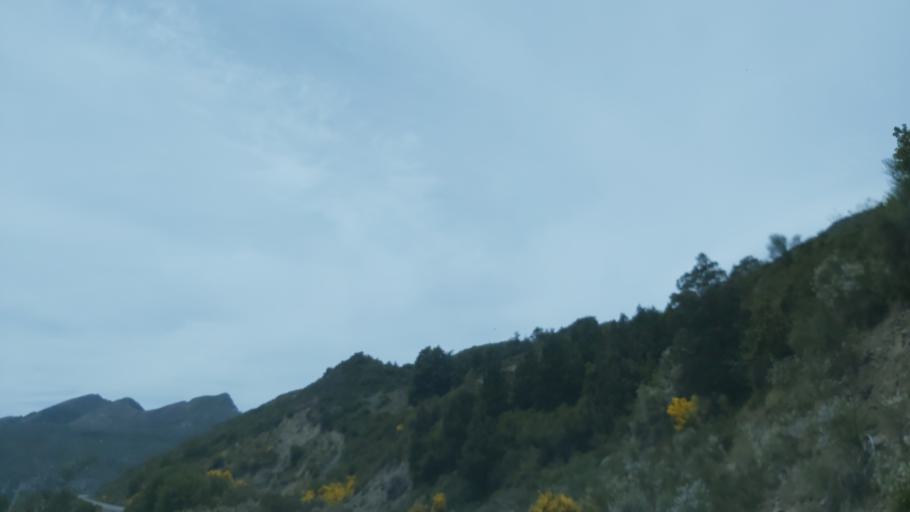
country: AR
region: Neuquen
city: Andacollo
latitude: -37.3917
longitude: -71.4031
